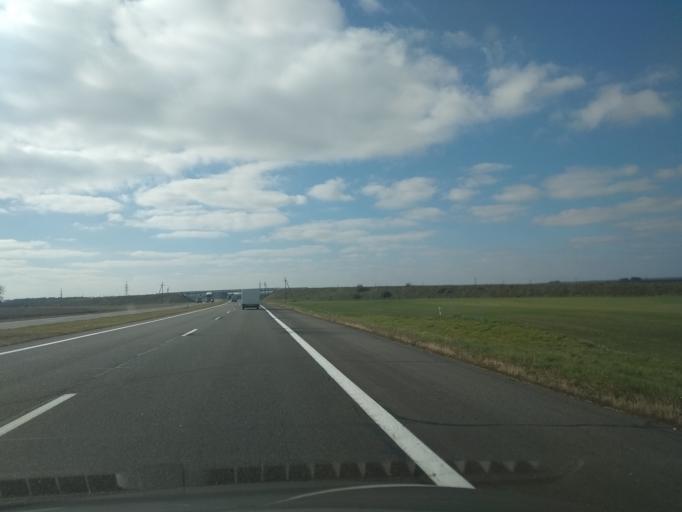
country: BY
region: Brest
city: Haradzishcha
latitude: 53.2373
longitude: 26.1817
